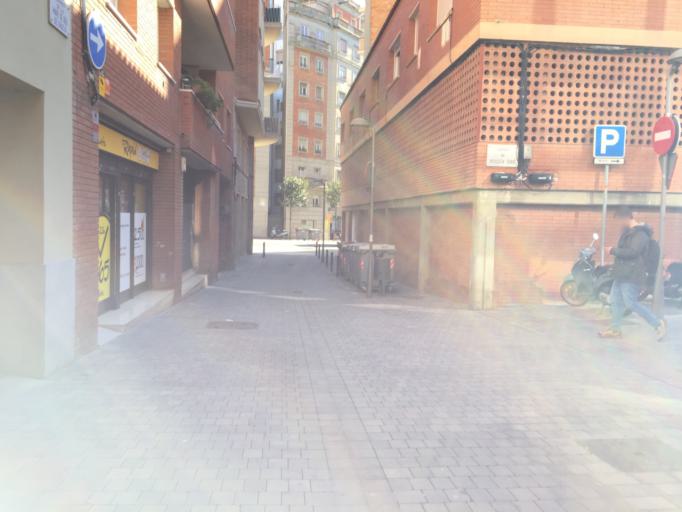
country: ES
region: Catalonia
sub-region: Provincia de Barcelona
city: Gracia
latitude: 41.4043
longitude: 2.1498
